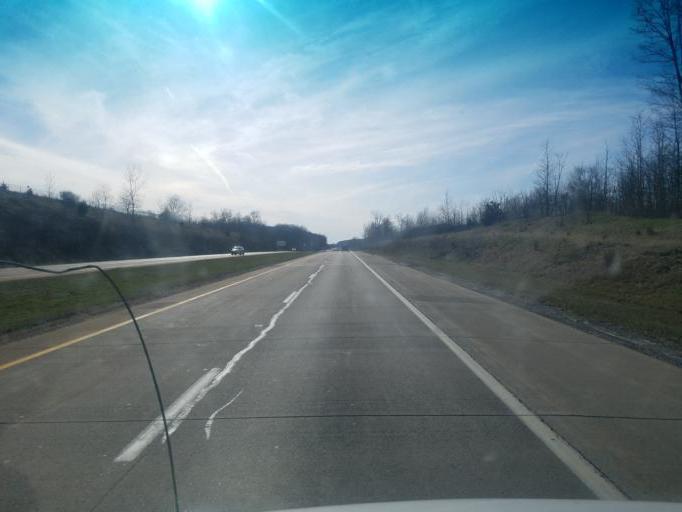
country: US
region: Ohio
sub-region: Champaign County
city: North Lewisburg
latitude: 40.3246
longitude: -83.5968
